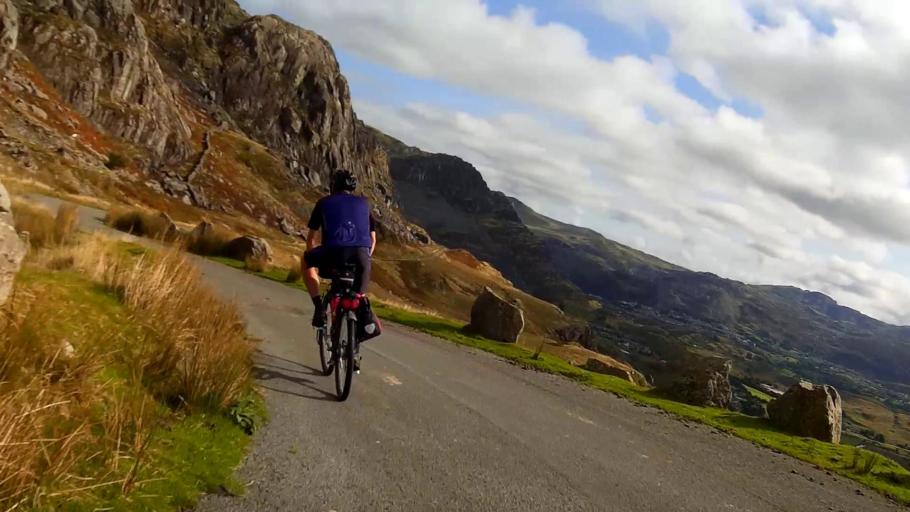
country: GB
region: Wales
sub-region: Gwynedd
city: Maentwrog
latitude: 52.9818
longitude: -3.9810
